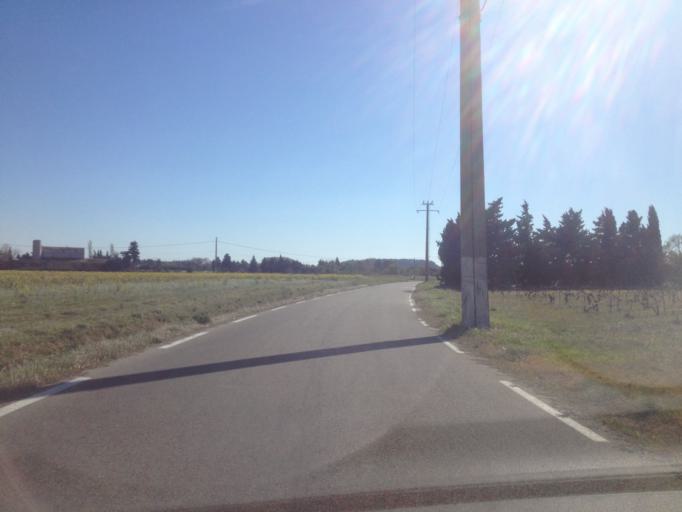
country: FR
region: Provence-Alpes-Cote d'Azur
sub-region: Departement du Vaucluse
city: Orange
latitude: 44.1562
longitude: 4.8272
